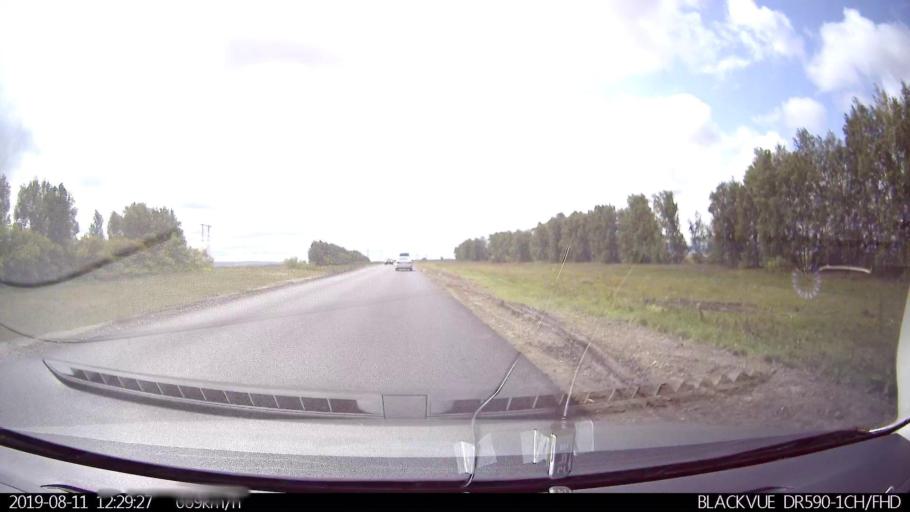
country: RU
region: Ulyanovsk
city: Ignatovka
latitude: 53.8345
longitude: 47.9025
